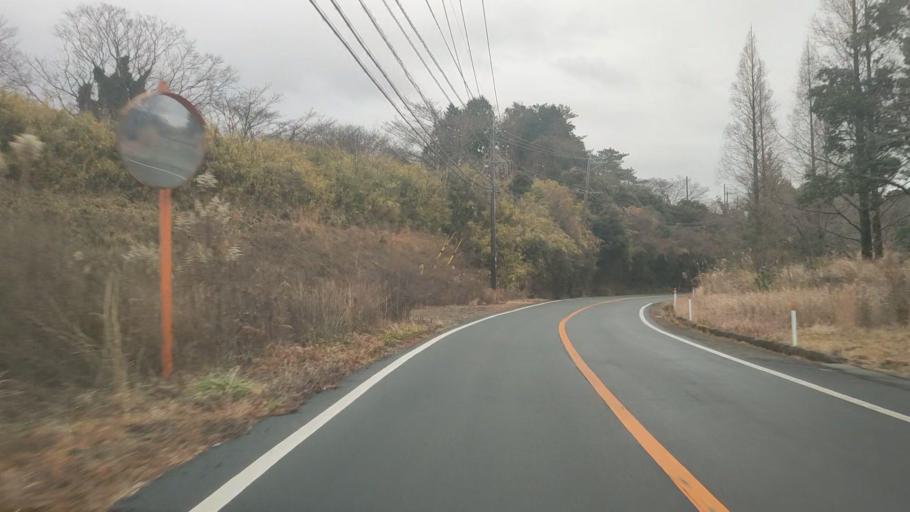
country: JP
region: Kumamoto
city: Aso
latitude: 32.8987
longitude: 131.0177
